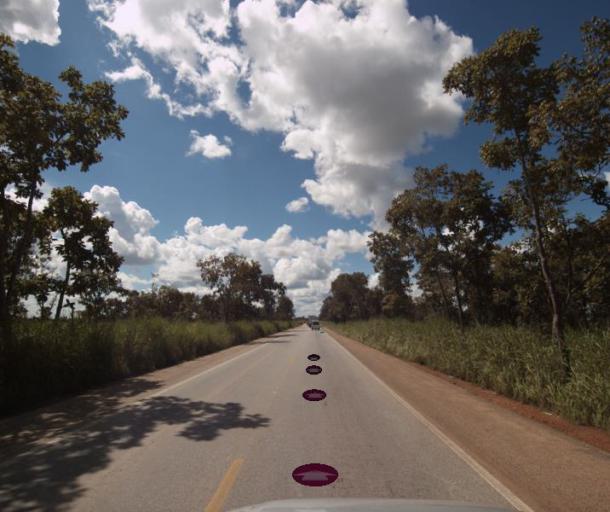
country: BR
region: Goias
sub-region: Porangatu
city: Porangatu
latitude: -13.6096
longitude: -49.0422
